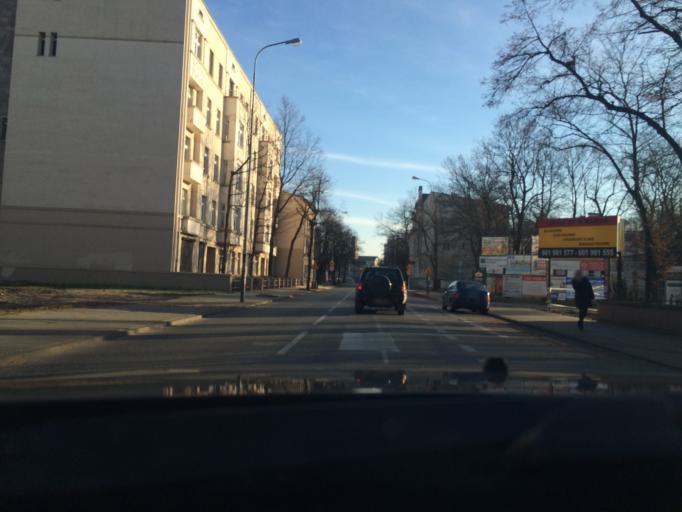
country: PL
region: Lodz Voivodeship
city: Lodz
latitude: 51.7628
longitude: 19.4399
